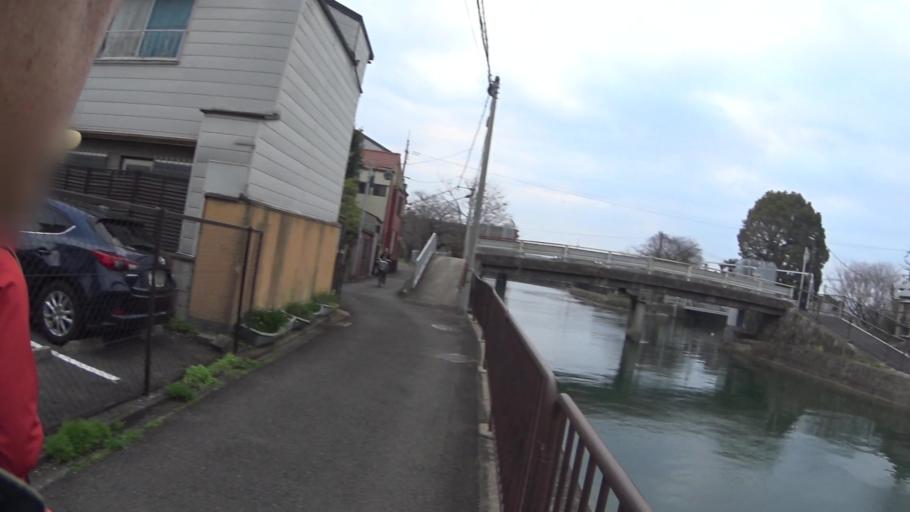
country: JP
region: Kyoto
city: Uji
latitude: 34.9462
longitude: 135.7680
